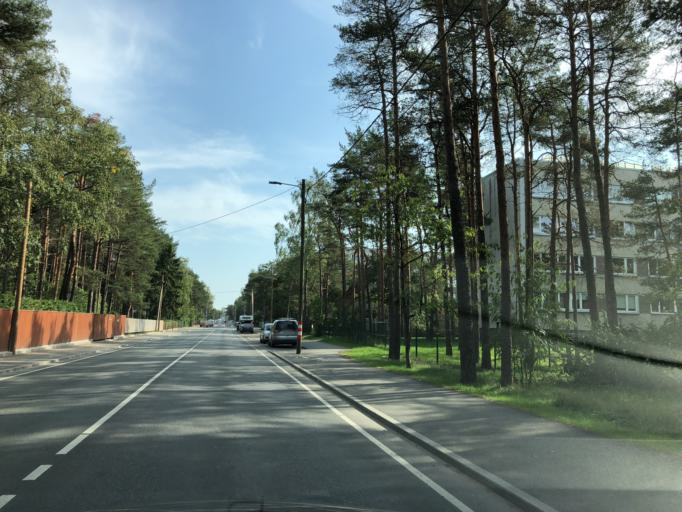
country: EE
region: Harju
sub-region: Tallinna linn
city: Tallinn
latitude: 59.3772
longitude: 24.7087
